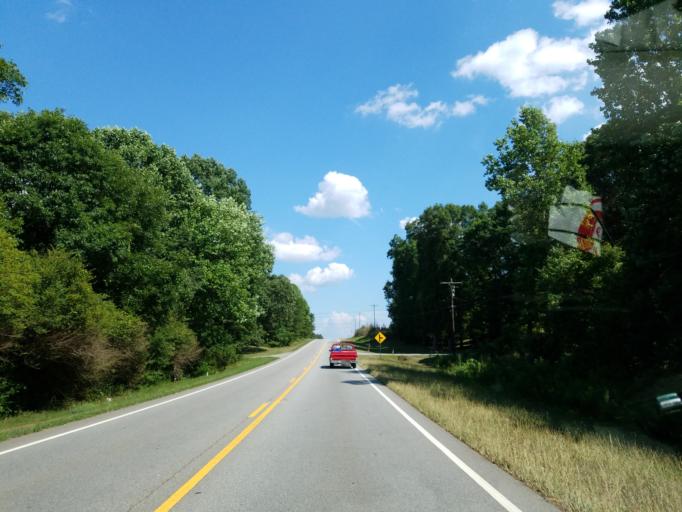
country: US
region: Georgia
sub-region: Lamar County
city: Barnesville
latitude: 33.0199
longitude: -84.1347
